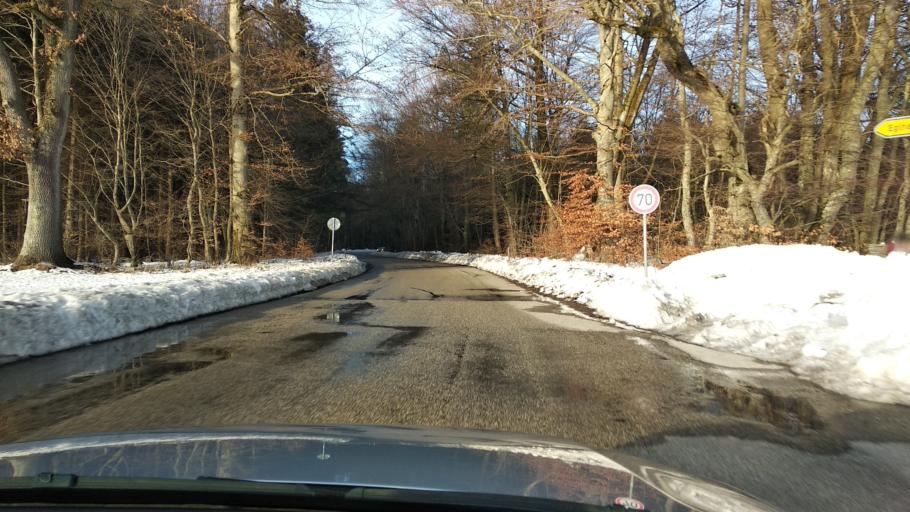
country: DE
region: Bavaria
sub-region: Upper Bavaria
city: Kirchseeon
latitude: 48.0670
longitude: 11.8556
